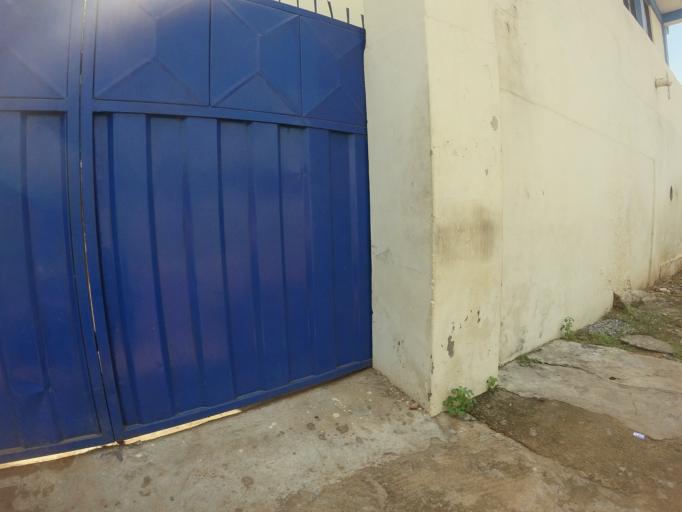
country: GH
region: Greater Accra
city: Gbawe
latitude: 5.6173
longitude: -0.3135
